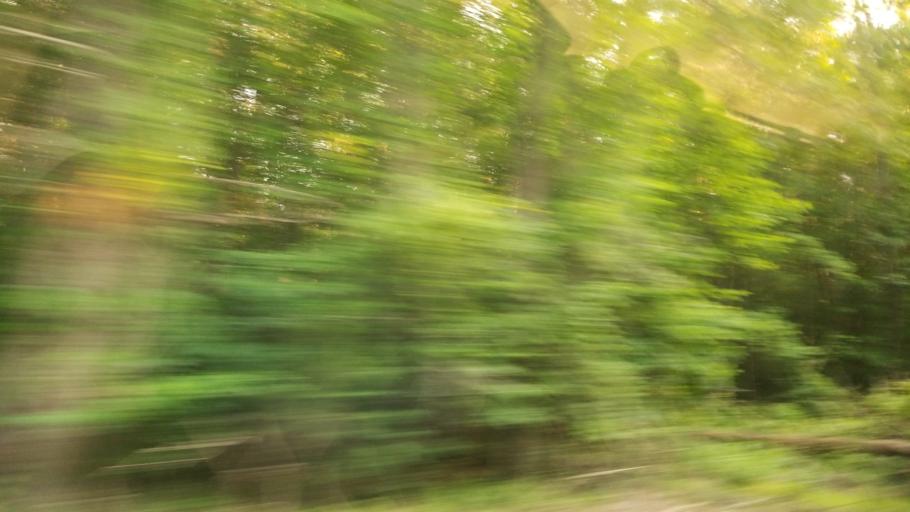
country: US
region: Virginia
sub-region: Fairfax County
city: Fairfax Station
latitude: 38.7952
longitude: -77.3542
